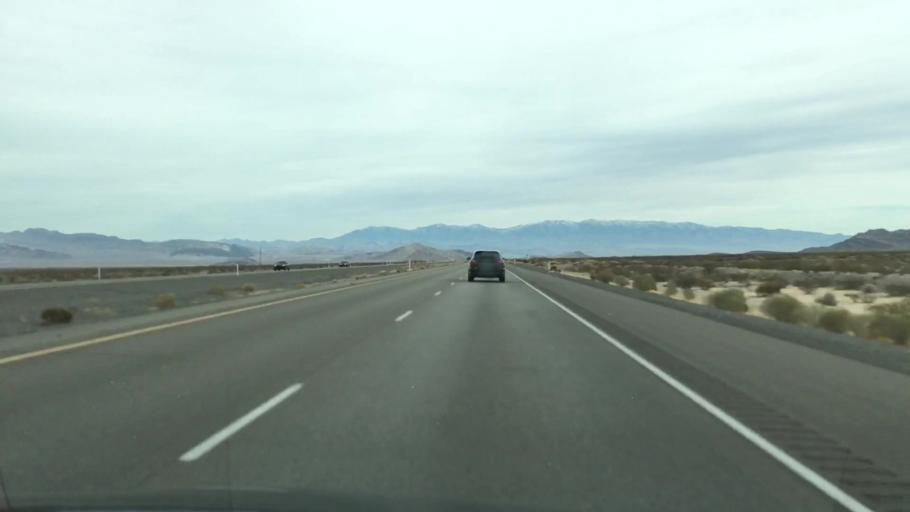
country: US
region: Nevada
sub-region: Nye County
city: Pahrump
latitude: 36.5741
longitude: -115.7533
